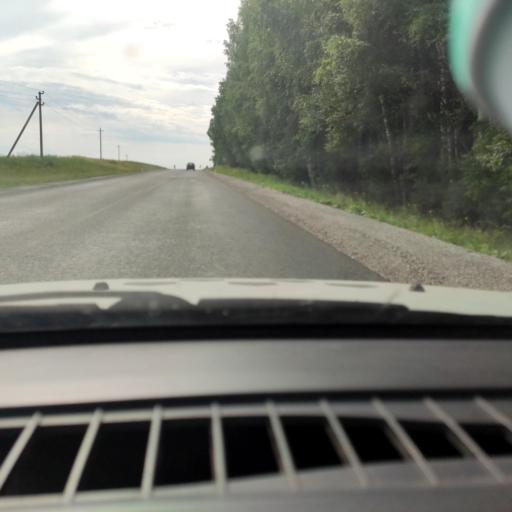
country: RU
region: Perm
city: Karagay
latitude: 58.2907
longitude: 54.8101
